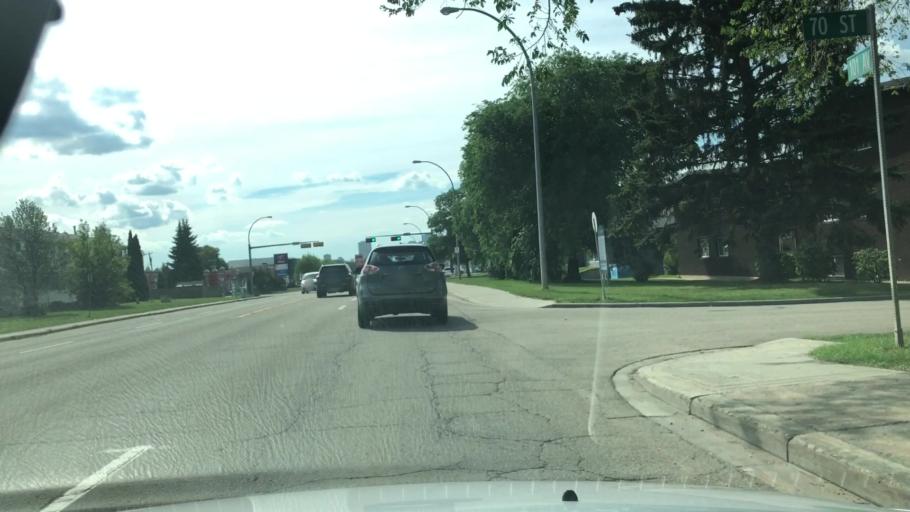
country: CA
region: Alberta
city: Edmonton
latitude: 53.5413
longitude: -113.4354
